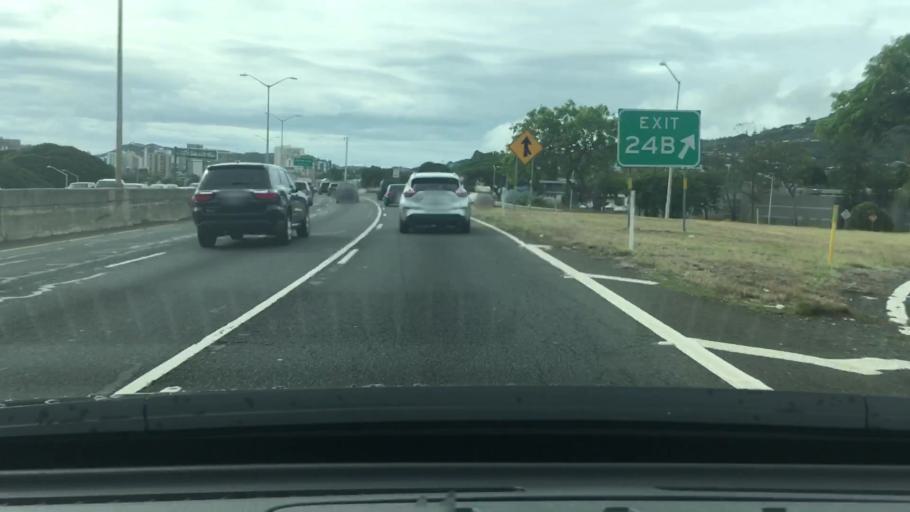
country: US
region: Hawaii
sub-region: Honolulu County
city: Honolulu
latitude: 21.2937
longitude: -157.8202
